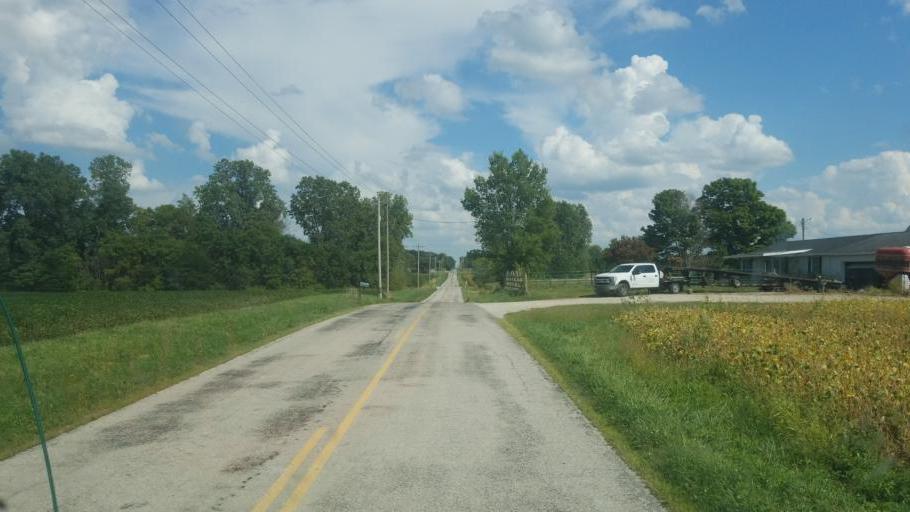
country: US
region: Ohio
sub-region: Seneca County
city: Tiffin
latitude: 40.9934
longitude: -83.1193
